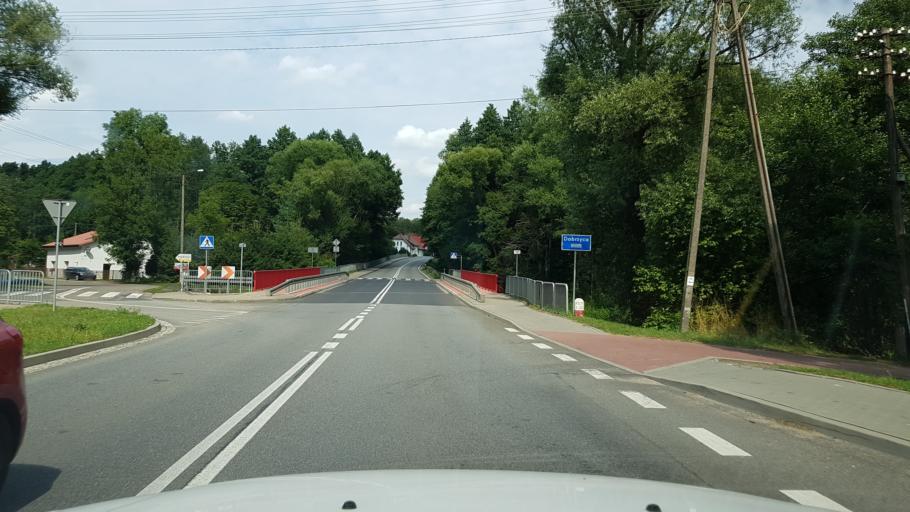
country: PL
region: West Pomeranian Voivodeship
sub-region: Powiat walecki
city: Walcz
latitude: 53.3021
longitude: 16.5306
